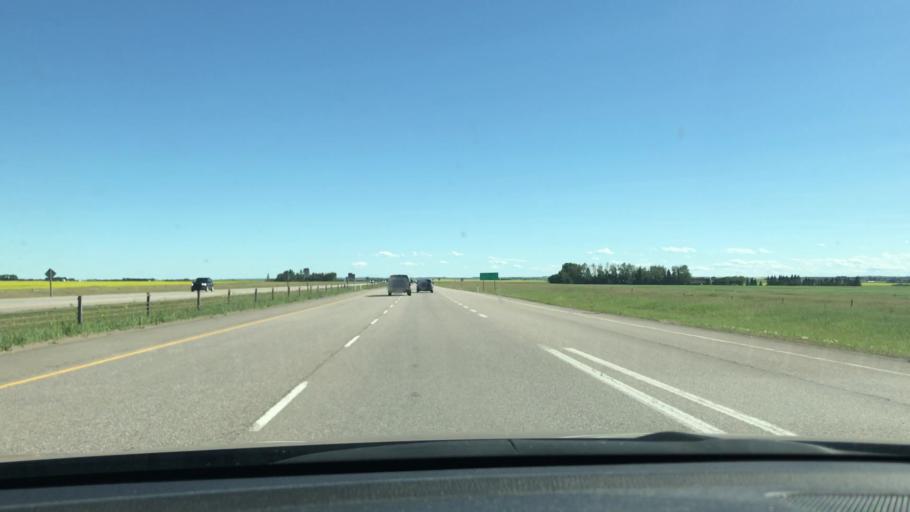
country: CA
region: Alberta
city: Didsbury
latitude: 51.6577
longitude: -114.0256
